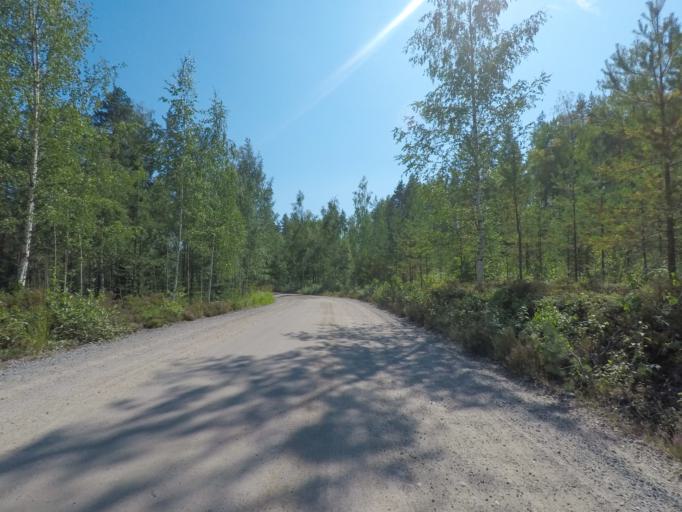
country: FI
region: Southern Savonia
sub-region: Mikkeli
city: Puumala
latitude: 61.4135
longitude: 28.0473
